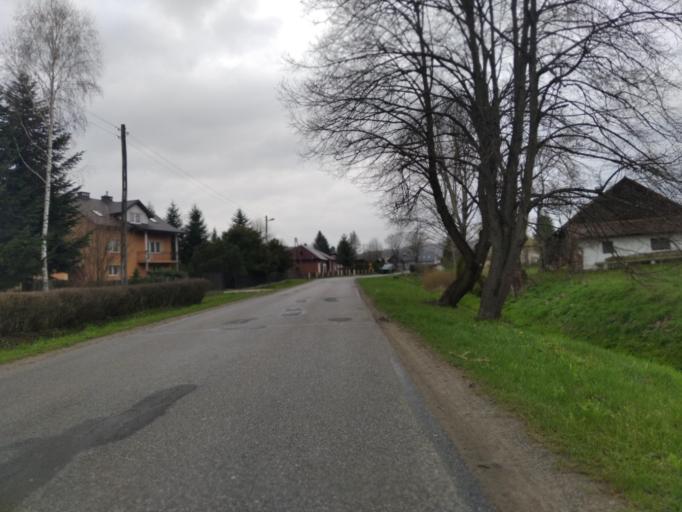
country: PL
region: Subcarpathian Voivodeship
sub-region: Powiat sanocki
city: Strachocina
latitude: 49.6081
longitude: 22.0849
